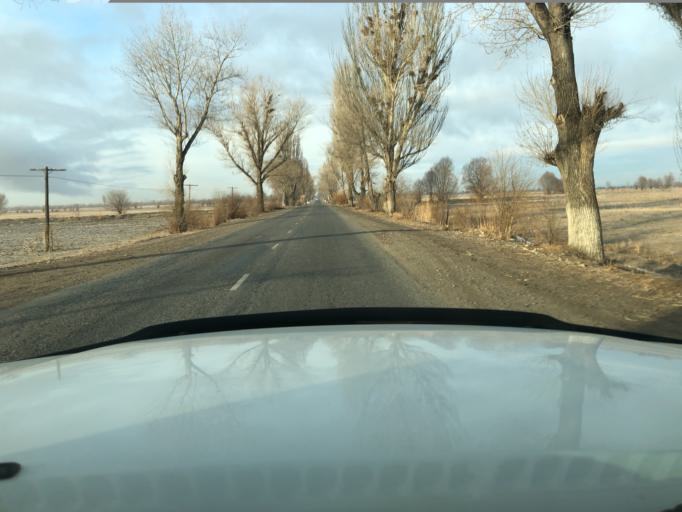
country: KG
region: Ysyk-Koel
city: Karakol
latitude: 42.4754
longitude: 78.3134
